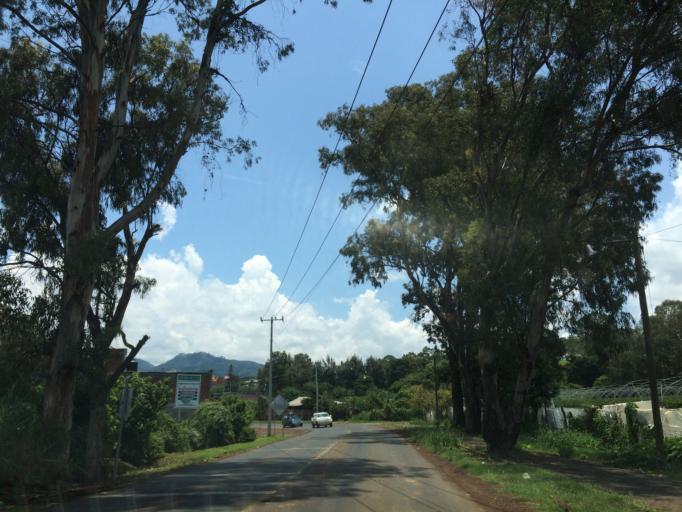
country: MX
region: Michoacan
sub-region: Periban
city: San Francisco Periban
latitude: 19.5498
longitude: -102.4000
